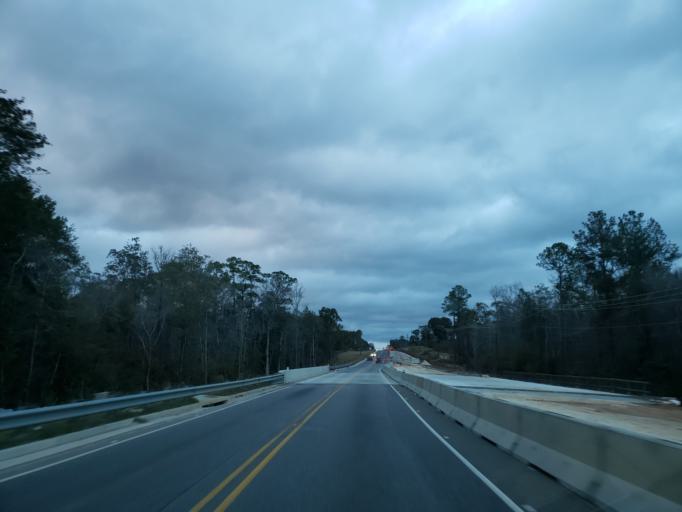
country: US
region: Alabama
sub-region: Mobile County
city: Chickasaw
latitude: 30.7802
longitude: -88.2258
